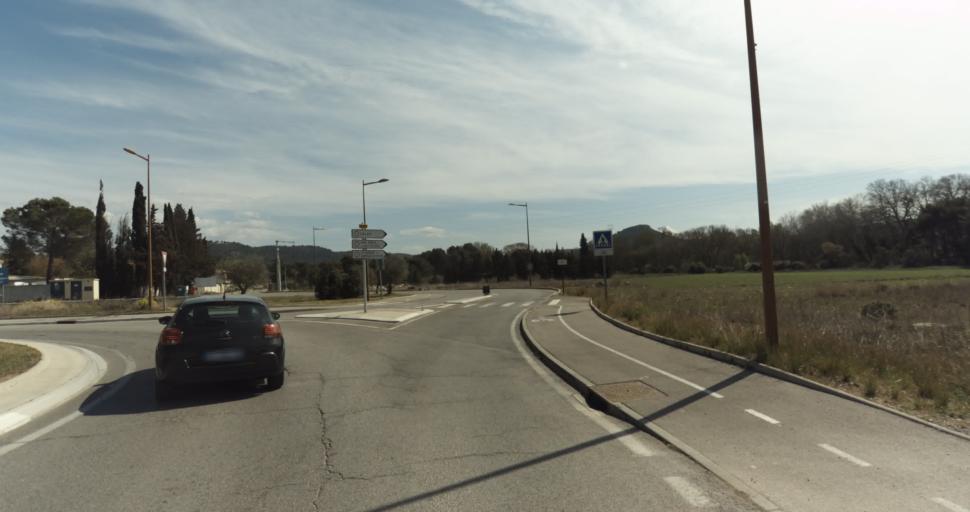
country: FR
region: Provence-Alpes-Cote d'Azur
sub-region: Departement des Bouches-du-Rhone
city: Velaux
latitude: 43.5400
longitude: 5.2670
